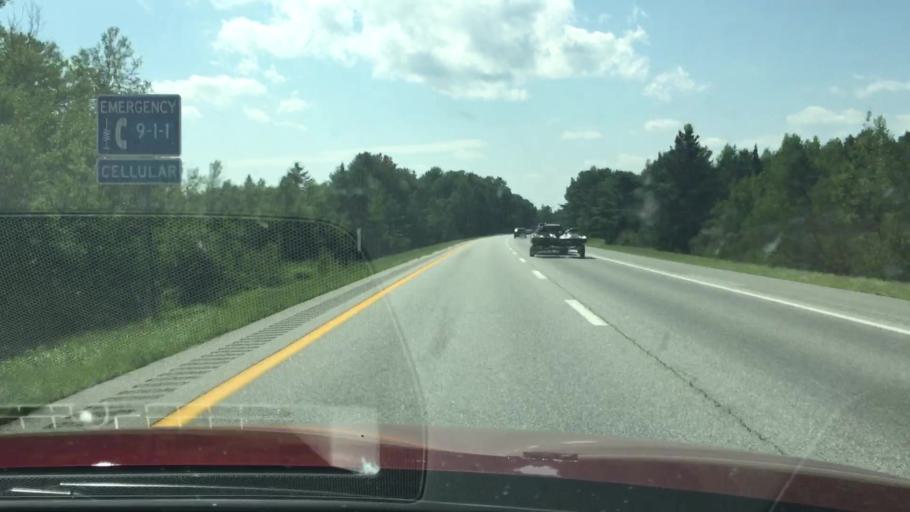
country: US
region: Maine
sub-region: Penobscot County
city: Hampden
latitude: 44.7701
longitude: -68.8754
